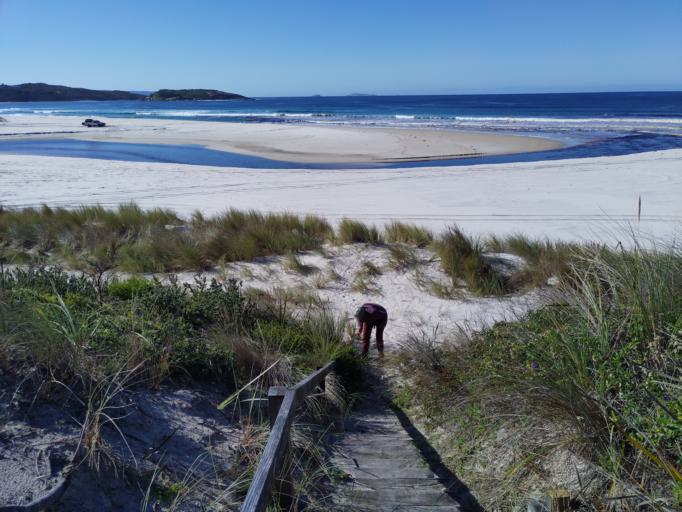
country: AU
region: Western Australia
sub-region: Albany
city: Grasmere
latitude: -35.0384
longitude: 117.6602
